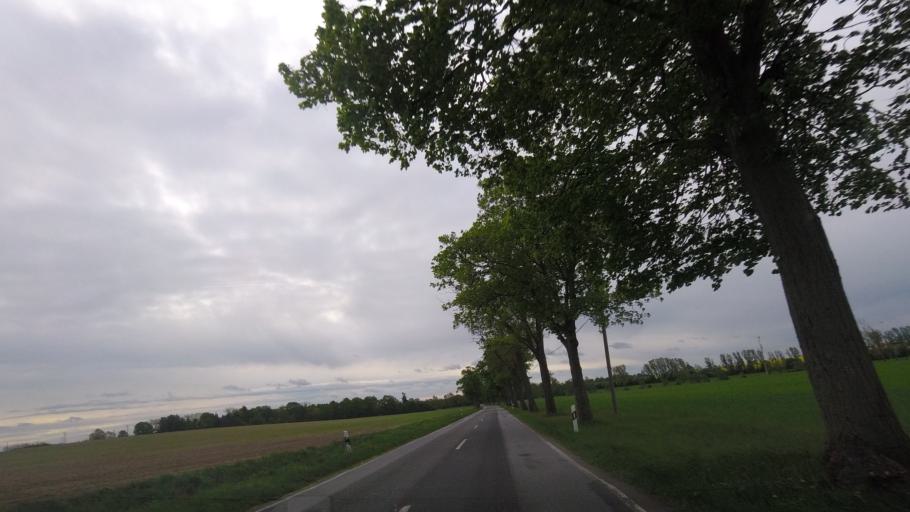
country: DE
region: Brandenburg
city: Dahme
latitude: 51.8916
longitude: 13.4145
